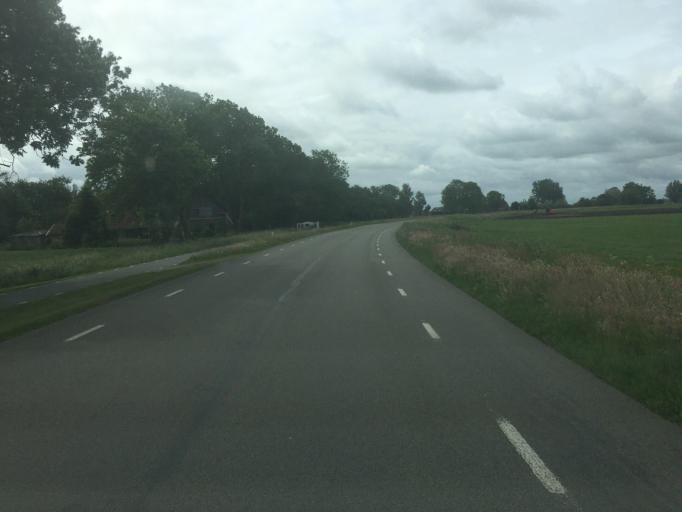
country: NL
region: Friesland
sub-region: Gemeente Lemsterland
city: Echtenerbrug
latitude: 52.8917
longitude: 5.8495
